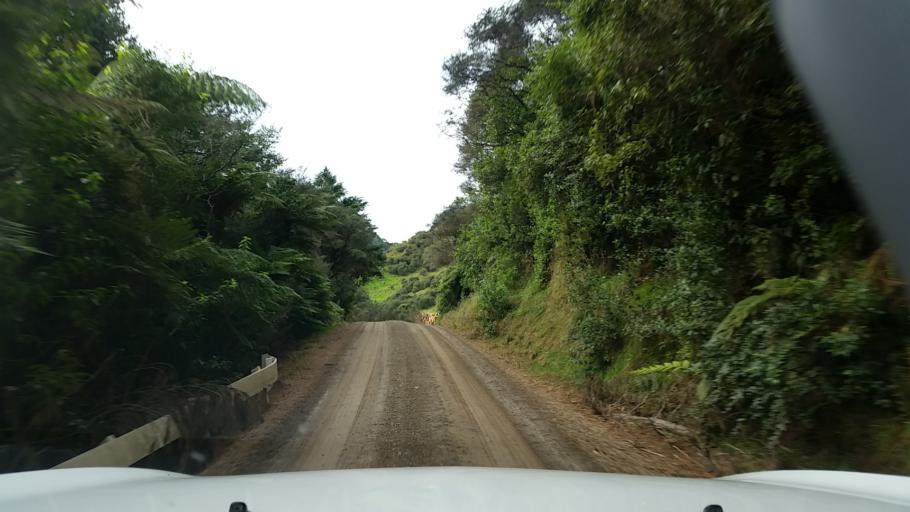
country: NZ
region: Taranaki
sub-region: New Plymouth District
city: Waitara
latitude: -38.8967
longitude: 174.7610
